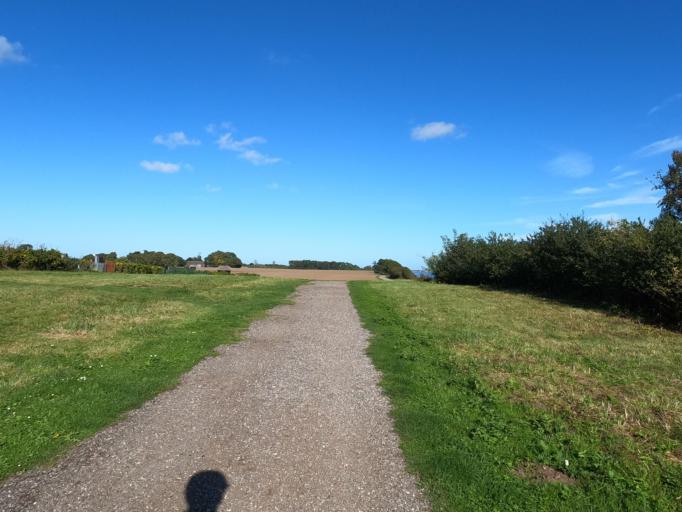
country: DE
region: Schleswig-Holstein
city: Neukirchen
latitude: 54.3085
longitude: 11.0747
